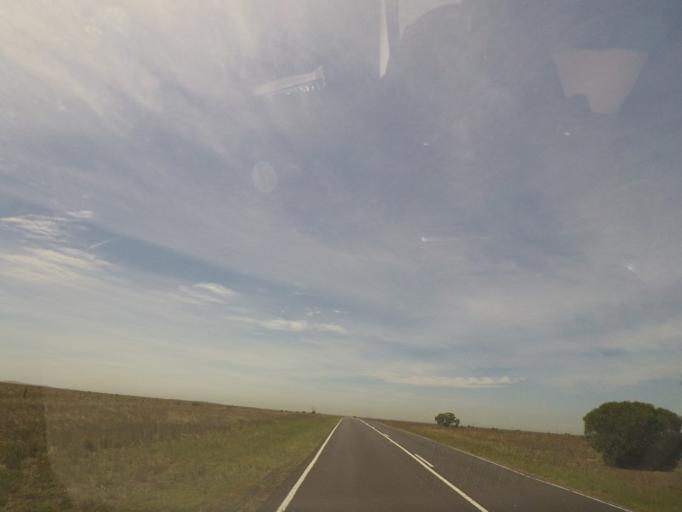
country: AU
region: Victoria
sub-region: Wyndham
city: Wyndham Vale
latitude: -37.7937
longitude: 144.4768
